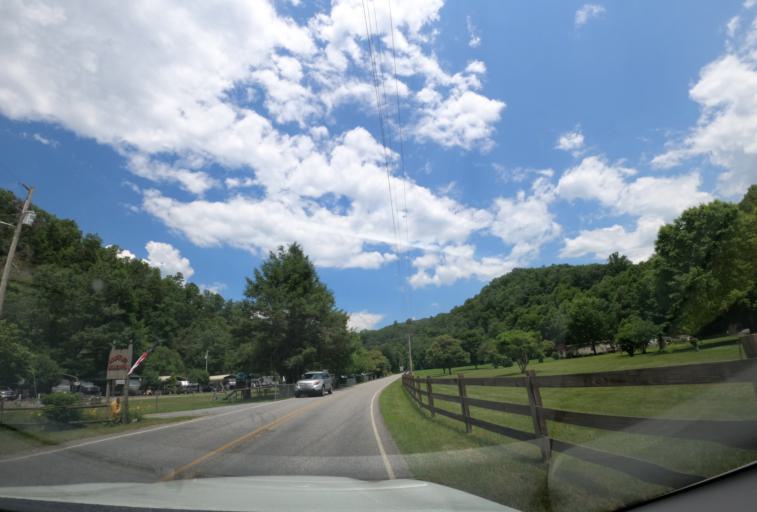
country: US
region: North Carolina
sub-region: Haywood County
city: Waynesville
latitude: 35.4350
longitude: -82.9257
